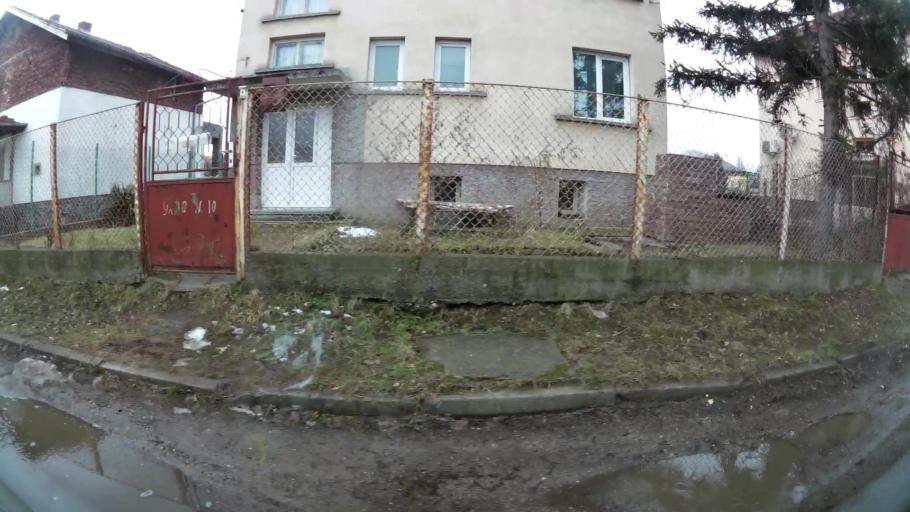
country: BG
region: Sofiya
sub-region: Obshtina Bozhurishte
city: Bozhurishte
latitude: 42.7421
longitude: 23.2682
